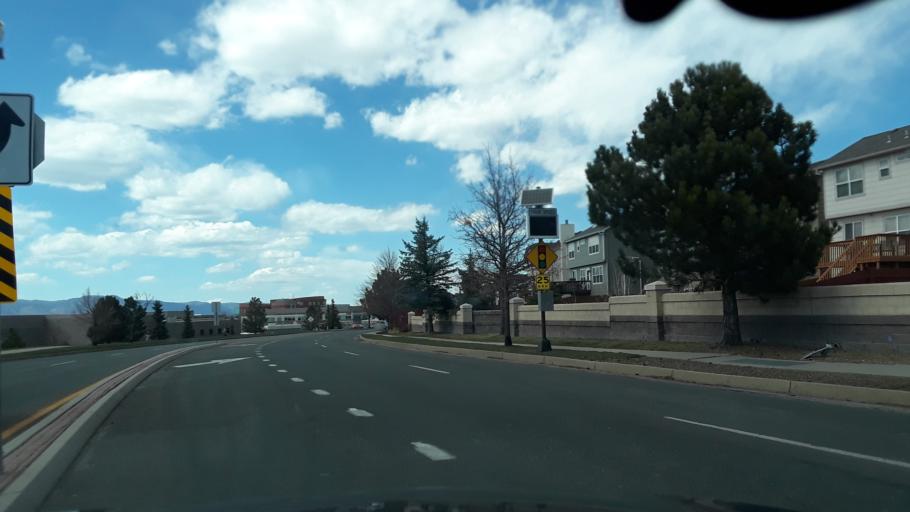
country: US
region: Colorado
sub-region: El Paso County
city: Black Forest
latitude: 38.9620
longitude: -104.7499
